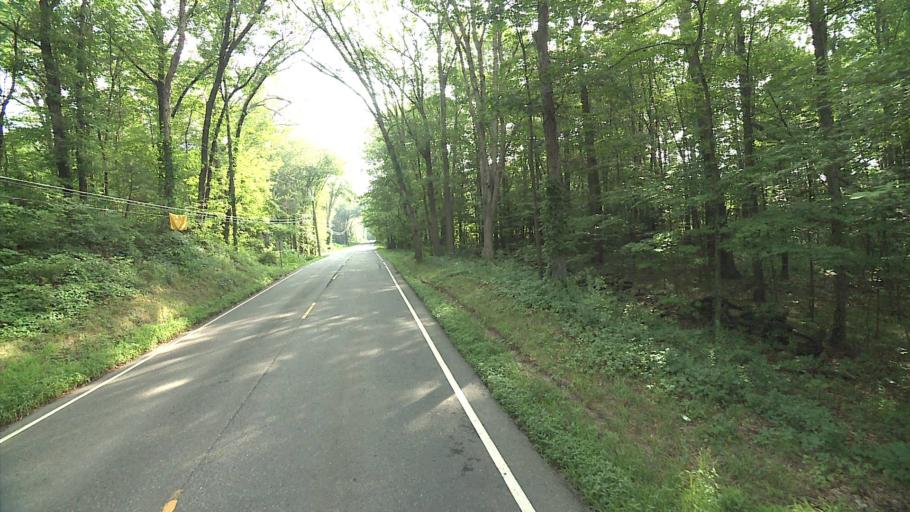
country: US
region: Connecticut
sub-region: Windham County
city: Quinebaug
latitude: 42.0019
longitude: -71.9788
